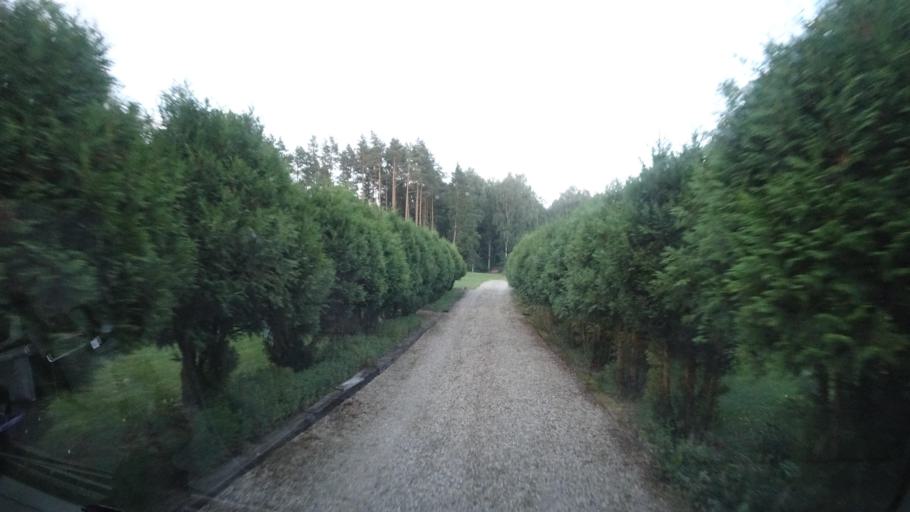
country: LT
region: Vilnius County
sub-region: Trakai
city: Rudiskes
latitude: 54.5075
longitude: 24.8898
